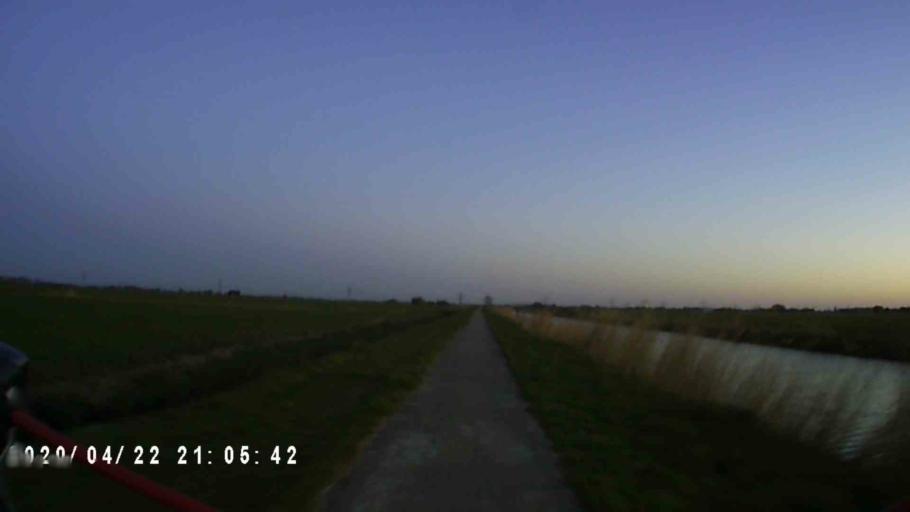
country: NL
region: Groningen
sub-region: Gemeente Winsum
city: Winsum
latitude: 53.3180
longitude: 6.5626
